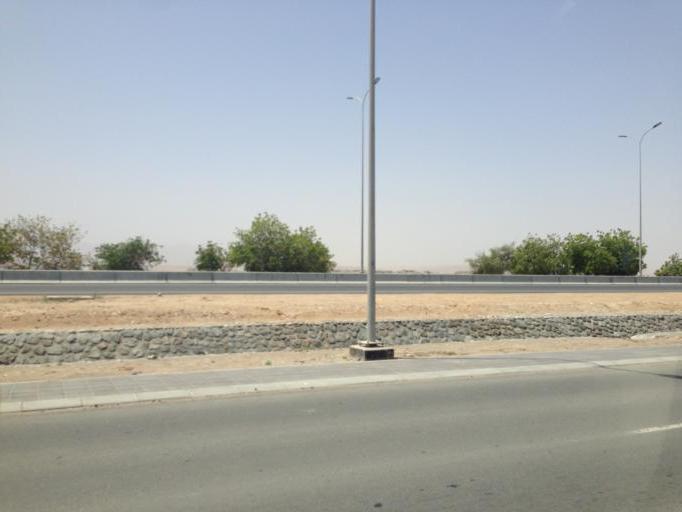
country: OM
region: Muhafazat Masqat
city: Bawshar
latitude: 23.6035
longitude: 58.3409
